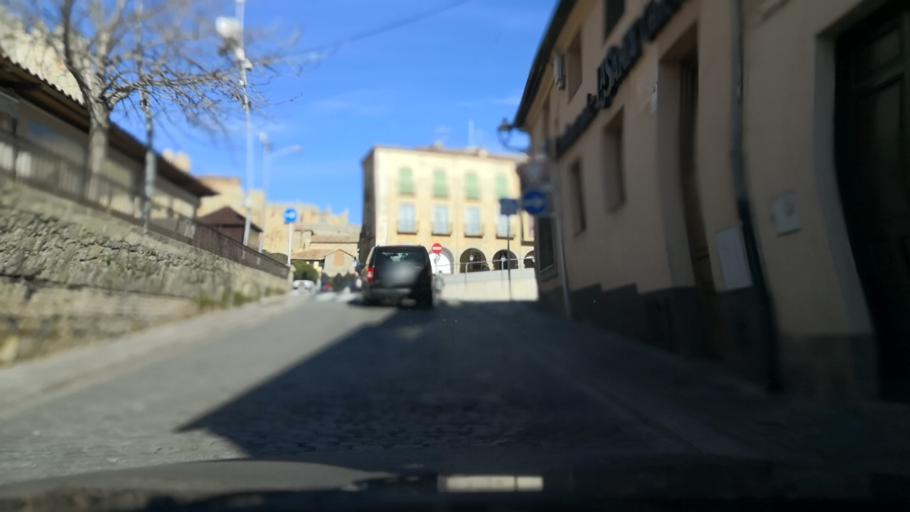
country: ES
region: Castille and Leon
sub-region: Provincia de Avila
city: Avila
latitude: 40.6539
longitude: -4.6970
